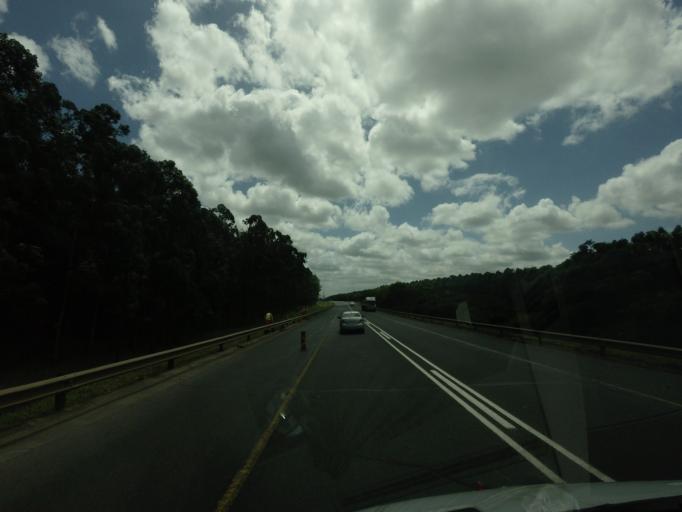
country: ZA
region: KwaZulu-Natal
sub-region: uThungulu District Municipality
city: KwaMbonambi
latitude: -28.5439
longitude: 32.1247
